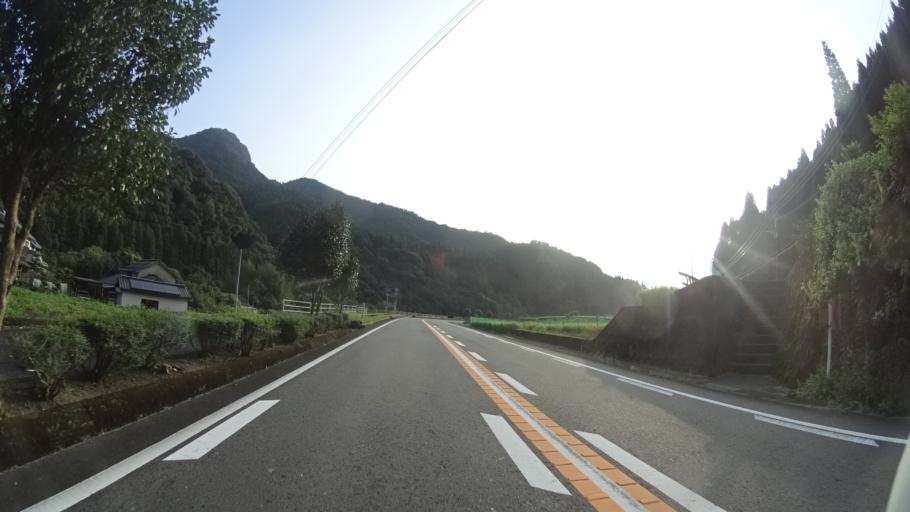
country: JP
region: Kumamoto
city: Minamata
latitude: 32.1647
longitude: 130.4719
